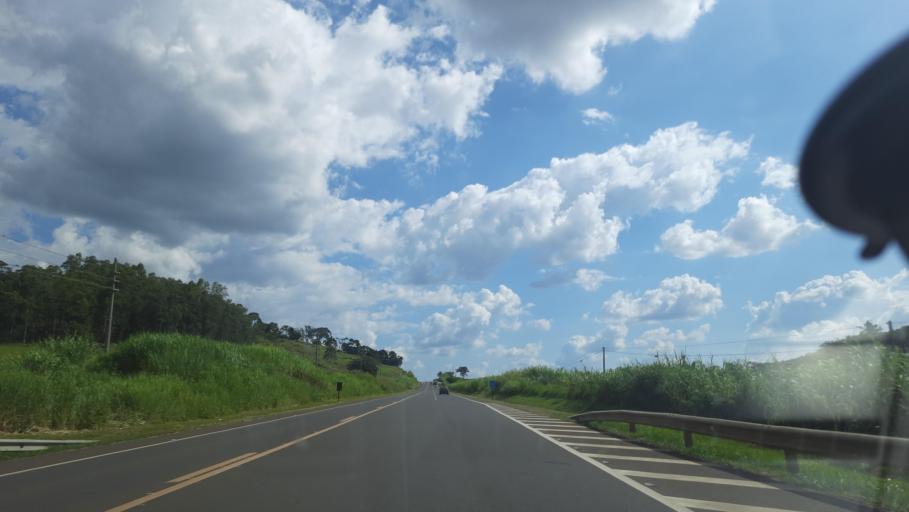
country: BR
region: Sao Paulo
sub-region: Sao Jose Do Rio Pardo
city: Sao Jose do Rio Pardo
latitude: -21.6524
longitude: -46.9118
